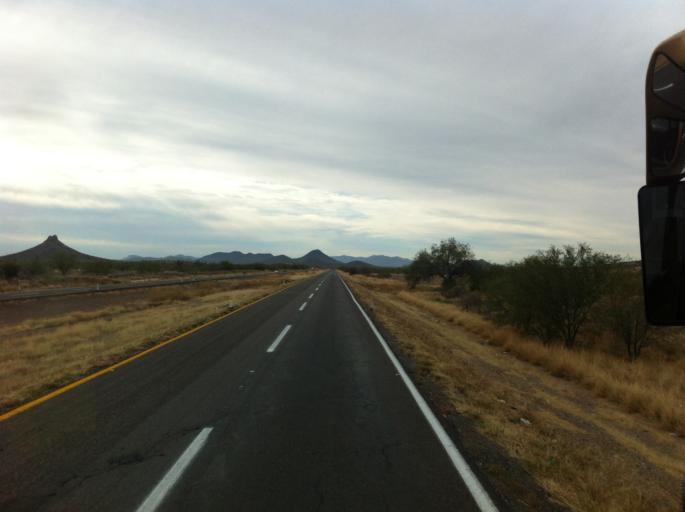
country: MX
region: Sonora
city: Hermosillo
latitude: 28.9158
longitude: -110.9522
